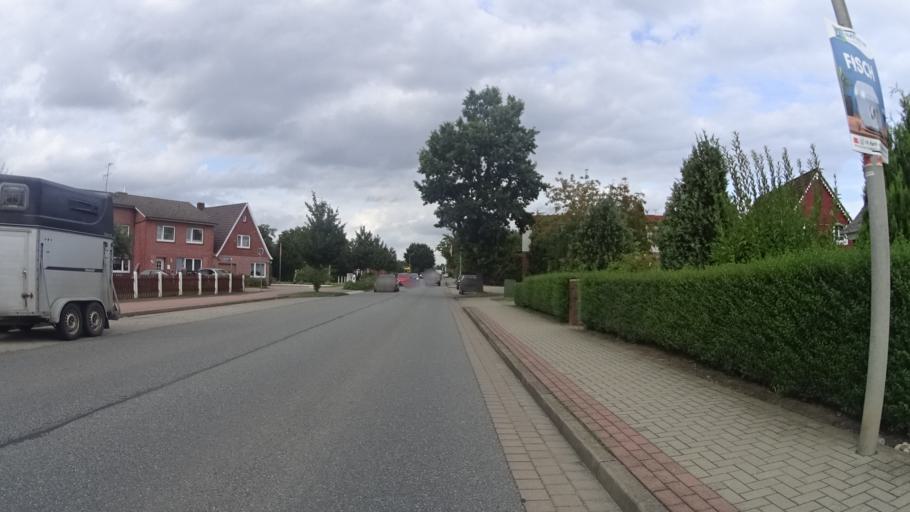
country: DE
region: Lower Saxony
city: Wischhafen
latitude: 53.7759
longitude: 9.3205
